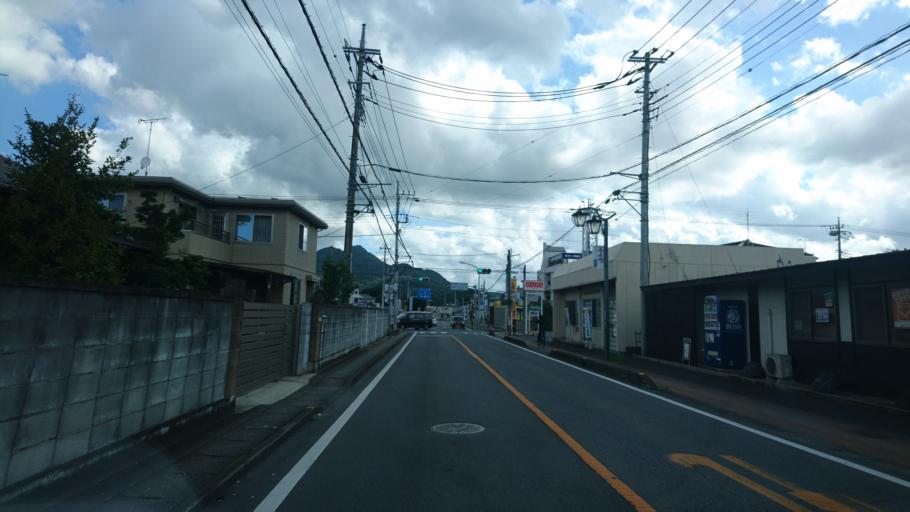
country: JP
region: Gunma
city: Kiryu
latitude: 36.4104
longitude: 139.3075
